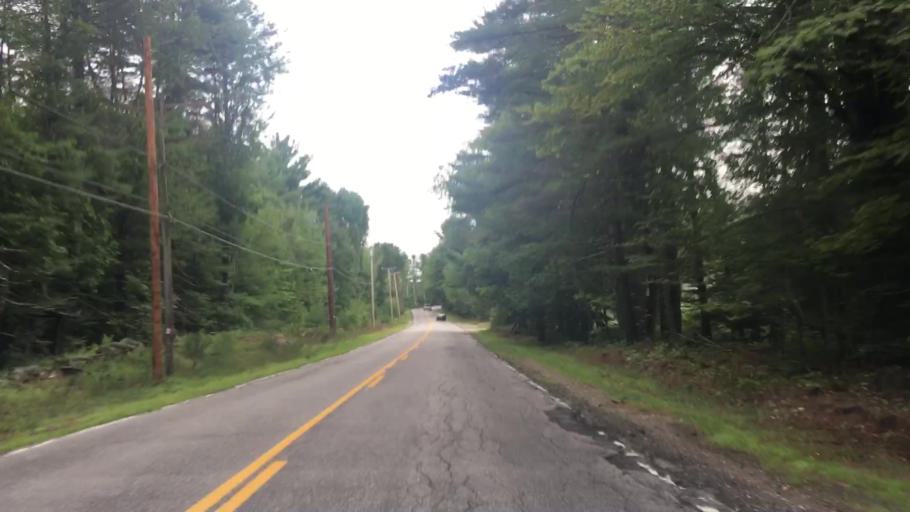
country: US
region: Maine
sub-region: York County
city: Lake Arrowhead
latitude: 43.6582
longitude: -70.7644
